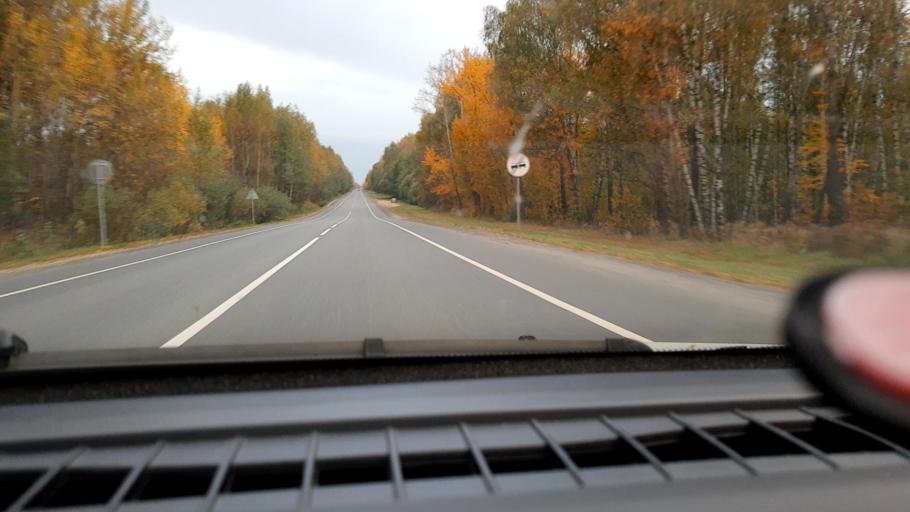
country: RU
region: Vladimir
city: Orgtrud
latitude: 56.2012
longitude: 40.7932
